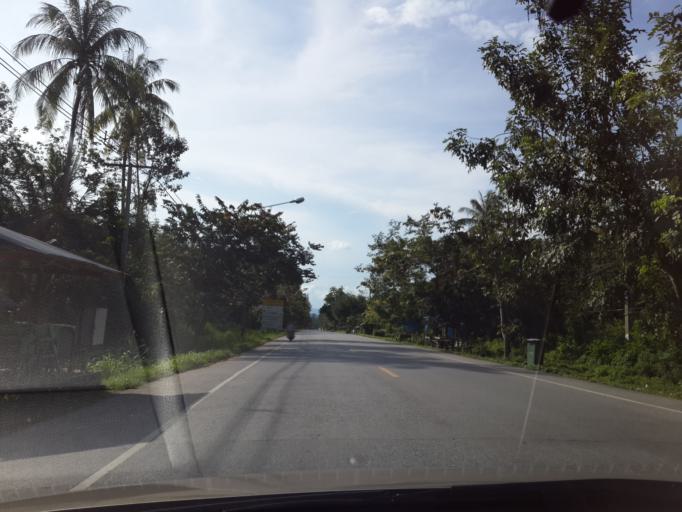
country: TH
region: Yala
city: Yala
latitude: 6.4985
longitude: 101.2945
